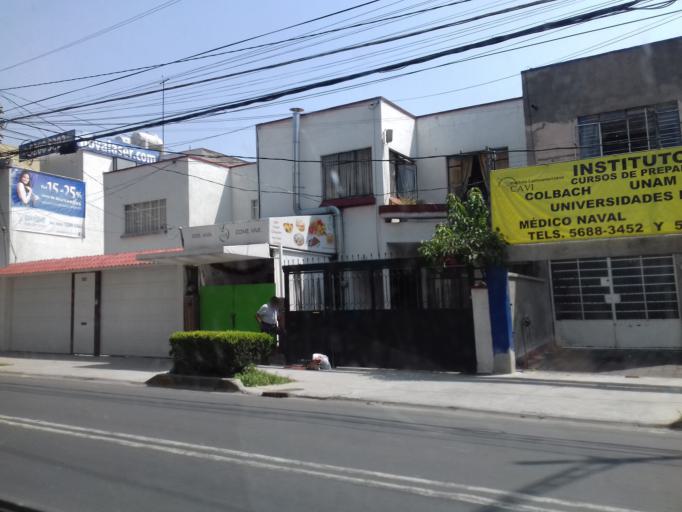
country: MX
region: Mexico City
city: Colonia del Valle
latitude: 19.3737
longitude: -99.1673
